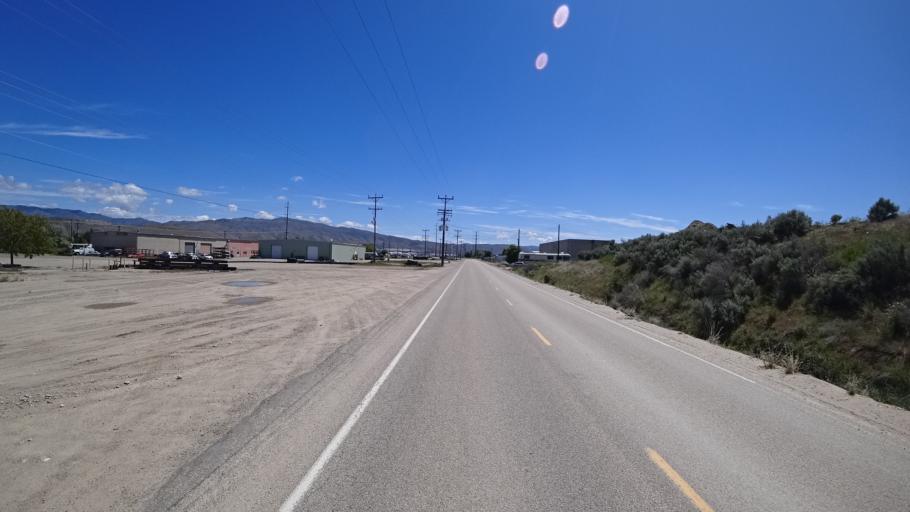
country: US
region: Idaho
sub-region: Ada County
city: Boise
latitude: 43.5605
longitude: -116.1779
